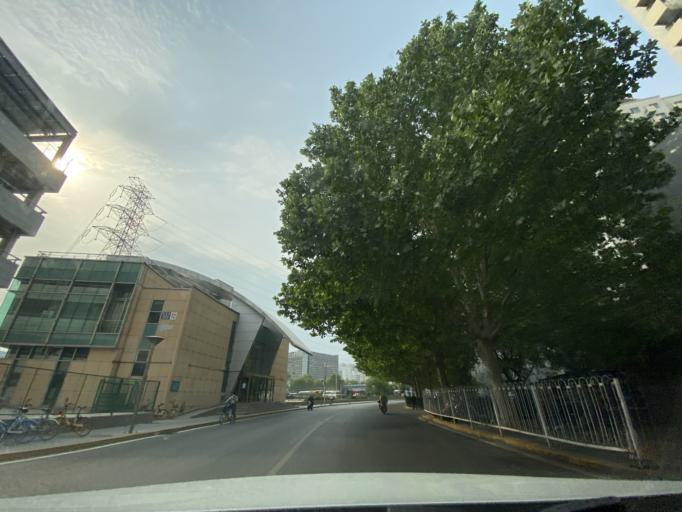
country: CN
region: Beijing
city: Haidian
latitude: 39.9761
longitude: 116.3360
